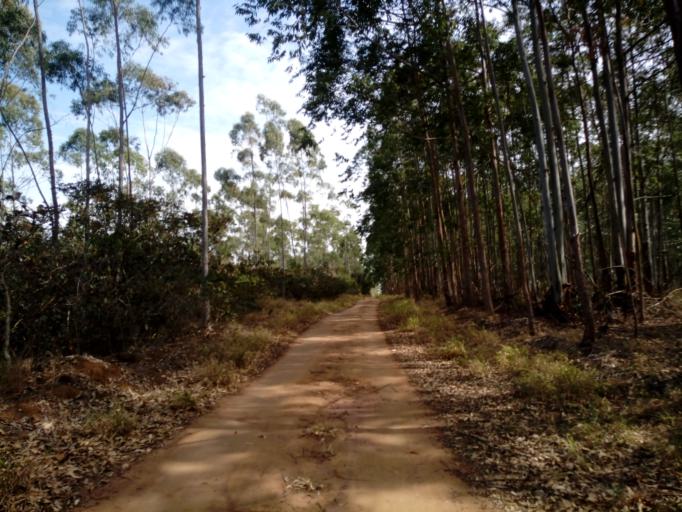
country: BR
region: Sao Paulo
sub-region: Sao Carlos
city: Sao Carlos
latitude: -21.9729
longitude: -47.8765
